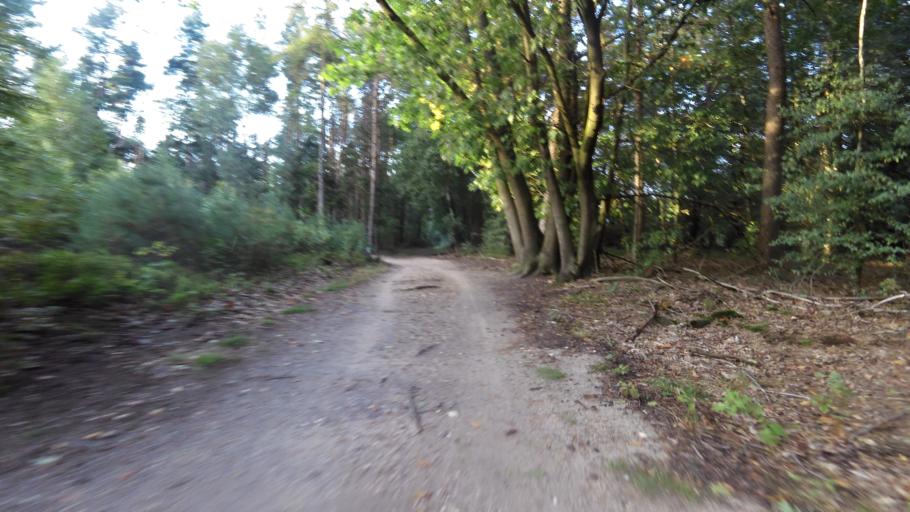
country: NL
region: Utrecht
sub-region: Gemeente Utrechtse Heuvelrug
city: Overberg
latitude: 51.9992
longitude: 5.5095
